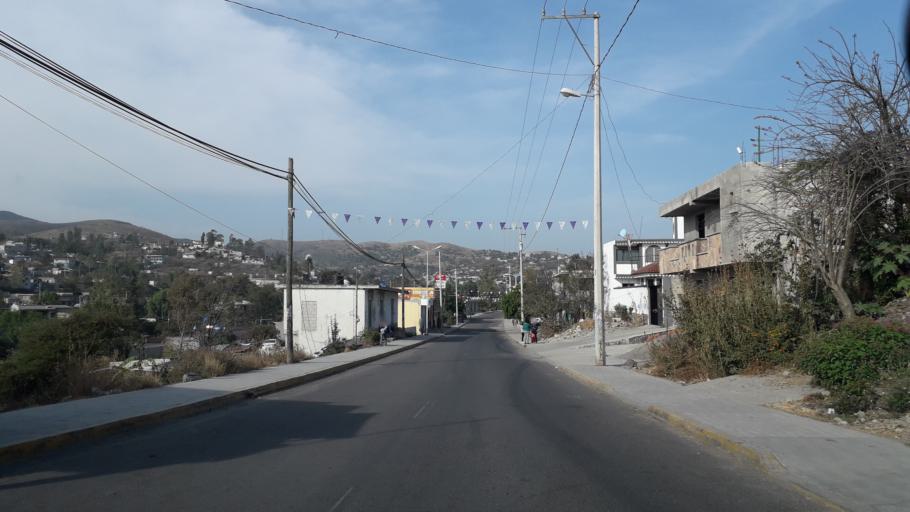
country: MX
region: Puebla
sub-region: Puebla
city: San Andres Azumiatla
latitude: 18.9053
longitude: -98.2464
